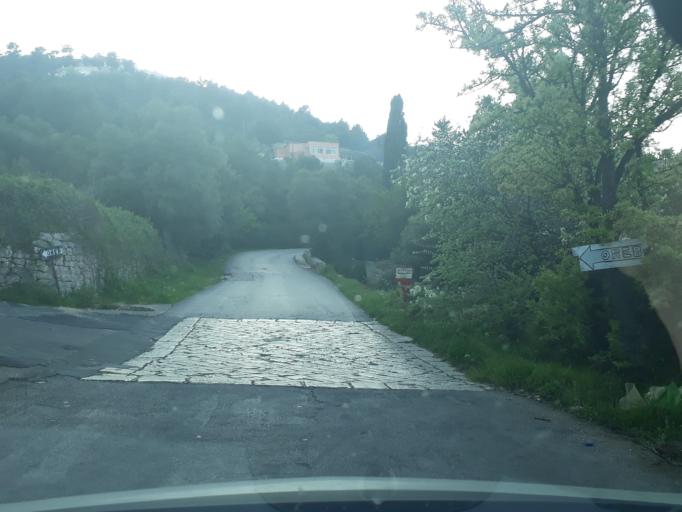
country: IT
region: Apulia
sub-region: Provincia di Brindisi
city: Lamie di Olimpie-Selva
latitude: 40.8297
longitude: 17.3404
